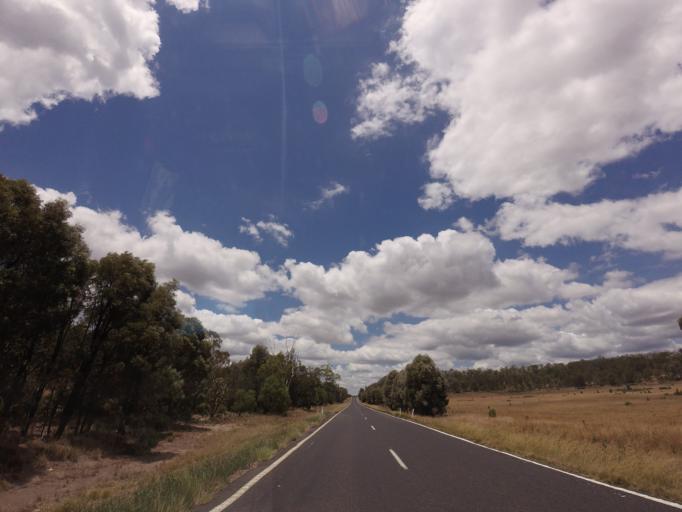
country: AU
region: Queensland
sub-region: Goondiwindi
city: Goondiwindi
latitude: -28.0368
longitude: 150.8119
